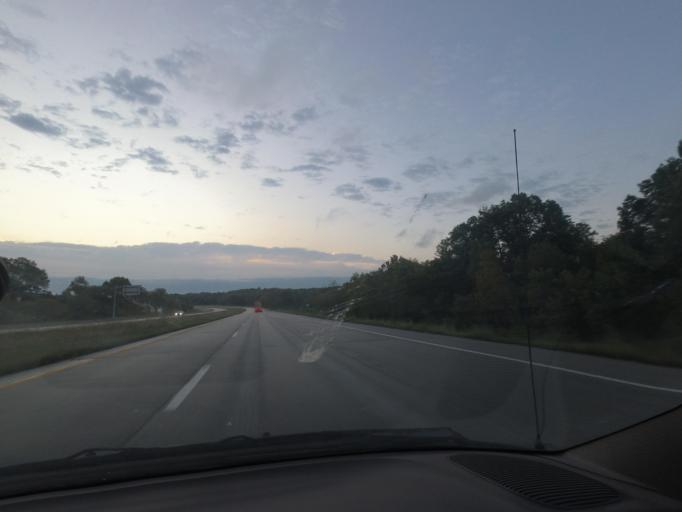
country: US
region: Missouri
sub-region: Macon County
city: Macon
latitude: 39.7475
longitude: -92.5000
